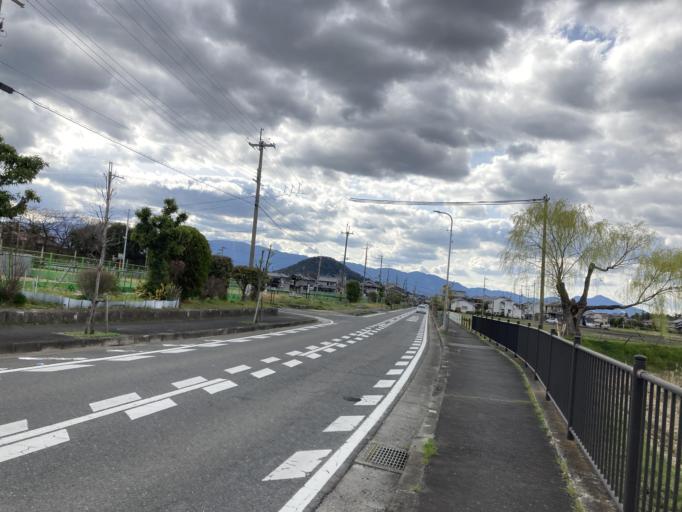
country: JP
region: Nara
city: Kashihara-shi
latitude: 34.4962
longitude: 135.8081
